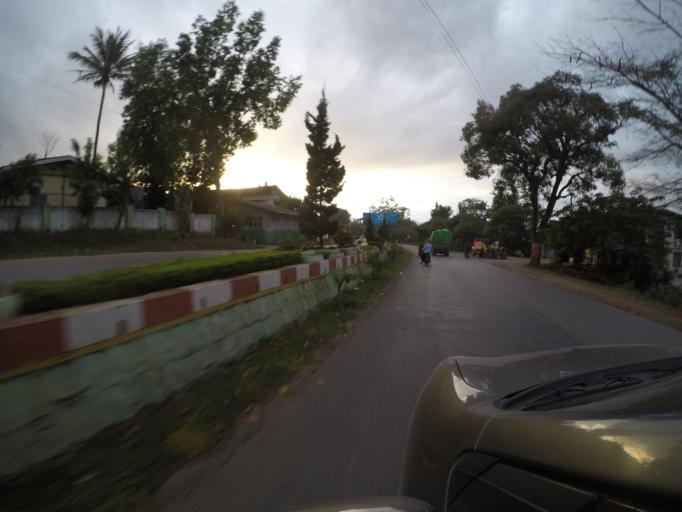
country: MM
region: Shan
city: Taunggyi
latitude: 20.7924
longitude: 97.0140
